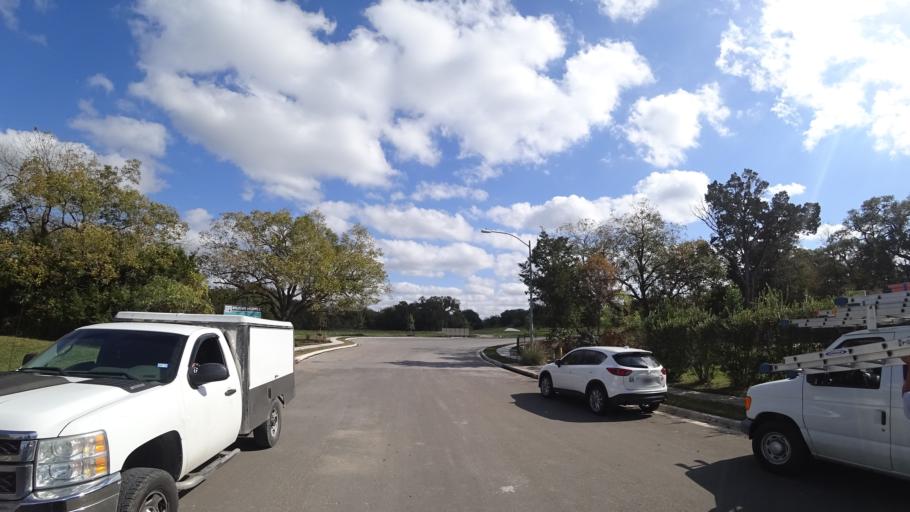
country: US
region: Texas
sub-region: Travis County
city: Barton Creek
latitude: 30.2467
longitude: -97.8957
